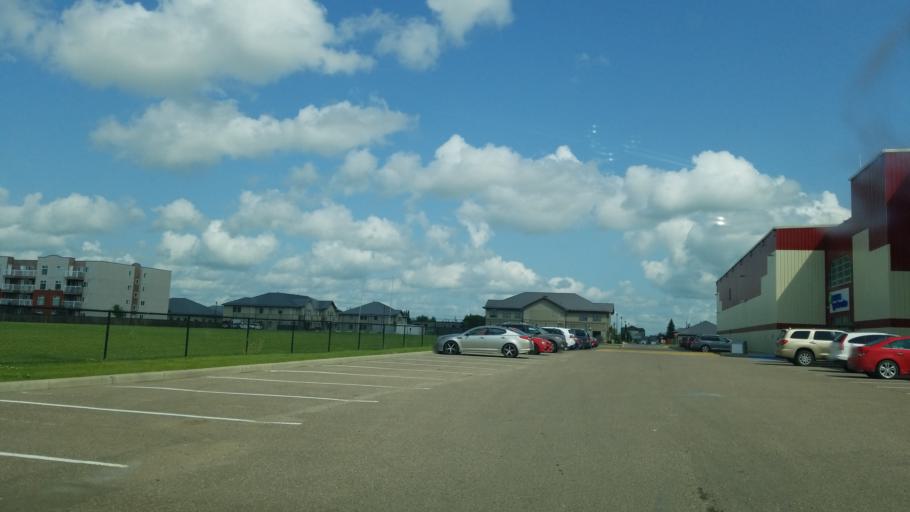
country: CA
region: Saskatchewan
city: Lloydminster
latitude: 53.2514
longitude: -110.0103
